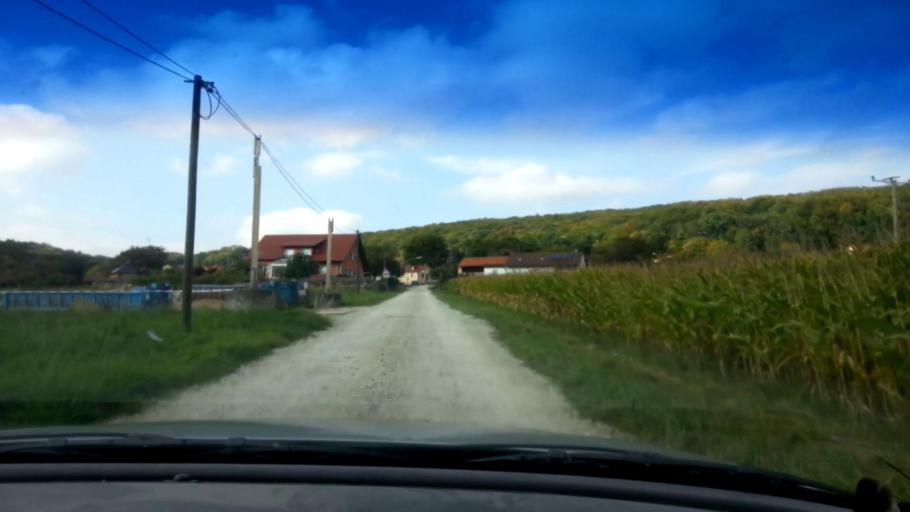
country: DE
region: Bavaria
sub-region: Upper Franconia
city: Schesslitz
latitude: 50.0089
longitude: 11.0453
